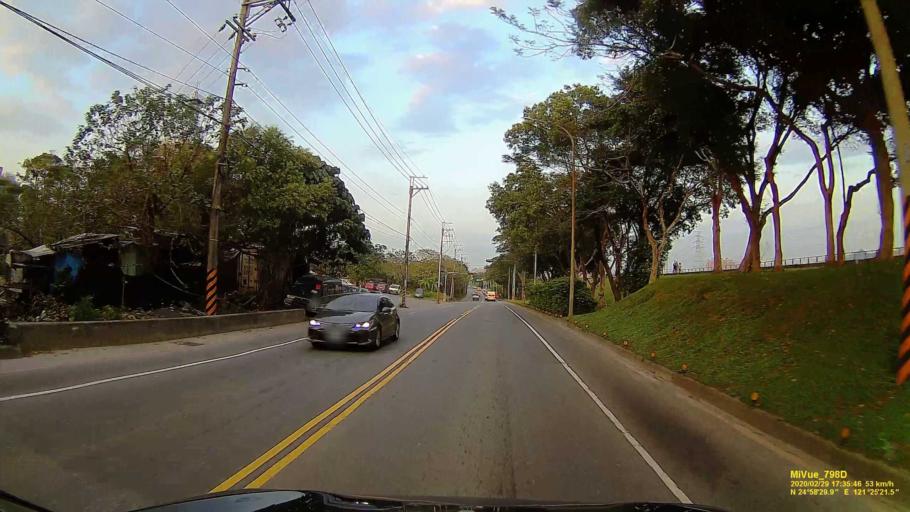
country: TW
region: Taipei
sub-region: Taipei
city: Banqiao
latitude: 24.9750
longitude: 121.4228
